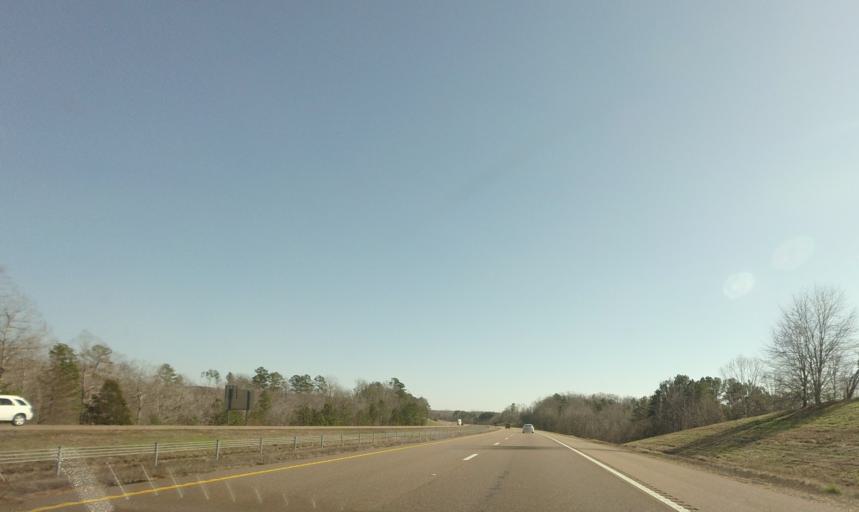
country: US
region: Mississippi
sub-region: Marshall County
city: Holly Springs
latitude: 34.6409
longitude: -89.2891
